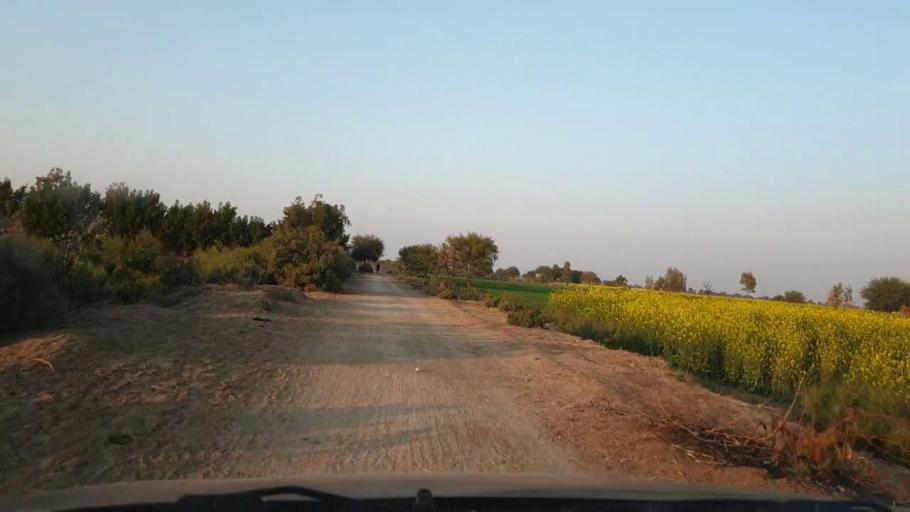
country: PK
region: Sindh
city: Jhol
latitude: 25.9235
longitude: 68.9428
